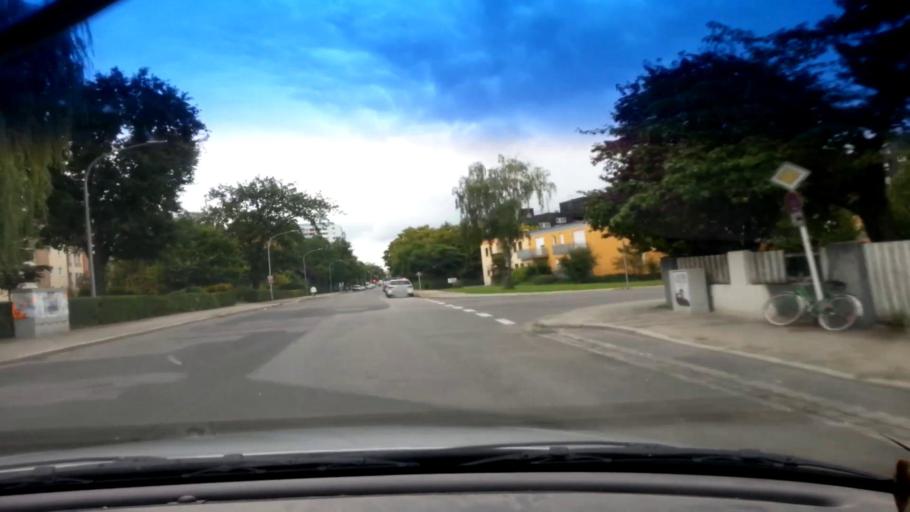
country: DE
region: Bavaria
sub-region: Upper Franconia
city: Bamberg
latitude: 49.9068
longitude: 10.9120
